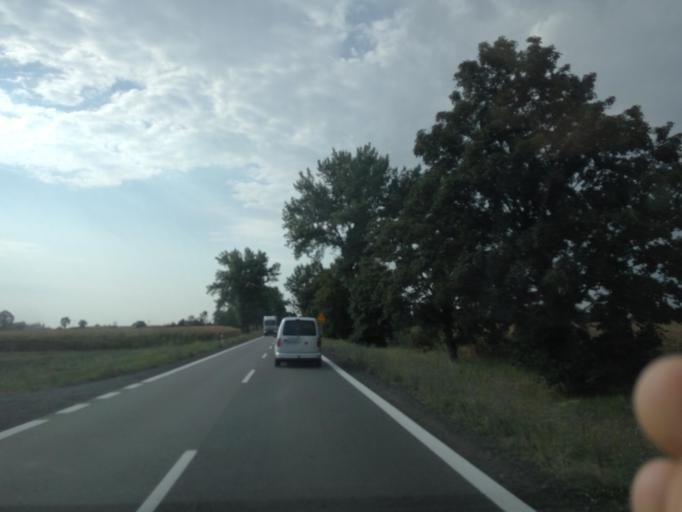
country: PL
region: Lower Silesian Voivodeship
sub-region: Powiat wroclawski
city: Zorawina
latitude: 50.9991
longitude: 17.0666
